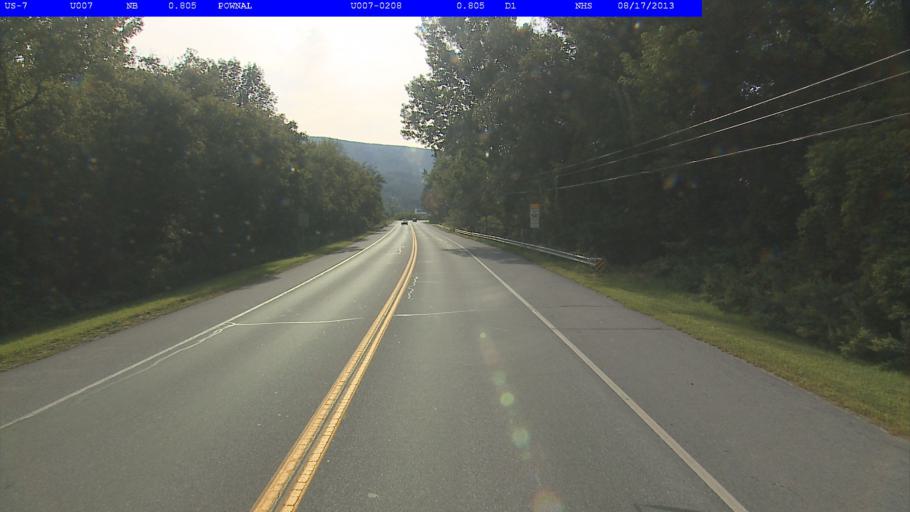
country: US
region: Massachusetts
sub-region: Berkshire County
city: Williamstown
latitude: 42.7540
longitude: -73.2208
